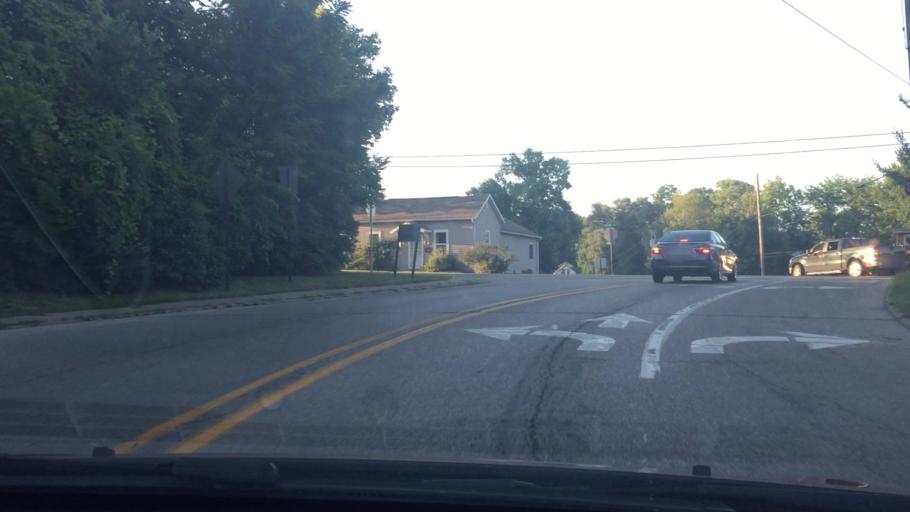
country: US
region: Iowa
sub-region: Muscatine County
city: Muscatine
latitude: 41.4190
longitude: -91.0597
